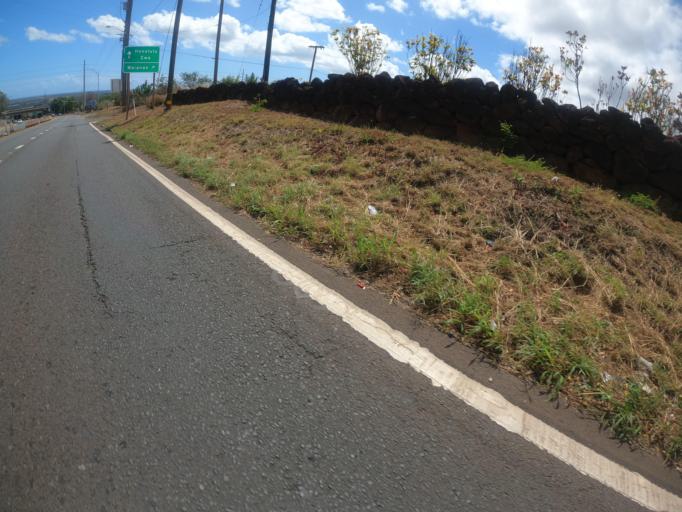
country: US
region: Hawaii
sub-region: Honolulu County
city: Royal Kunia
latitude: 21.3860
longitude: -158.0336
